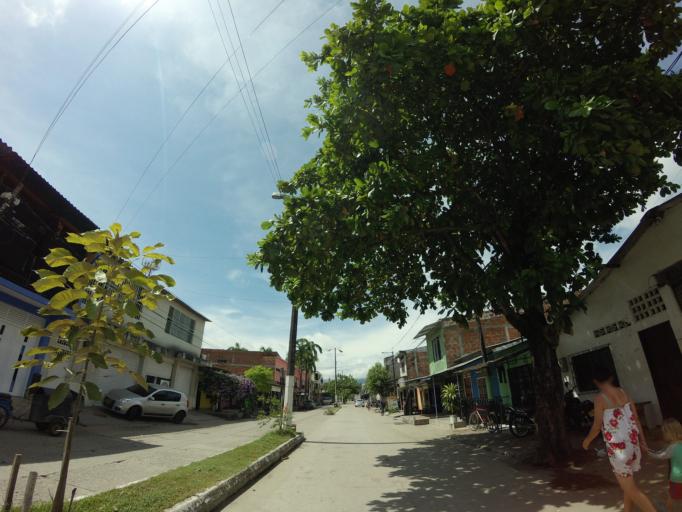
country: CO
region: Cundinamarca
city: Puerto Salgar
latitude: 5.4786
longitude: -74.6751
